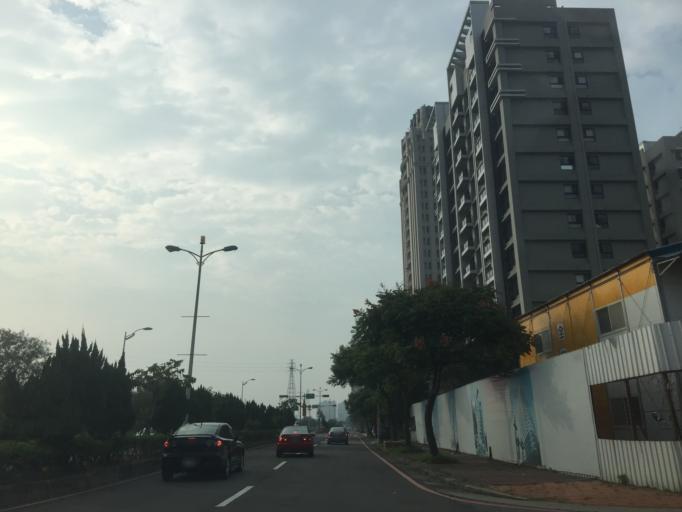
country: TW
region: Taiwan
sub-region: Hsinchu
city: Zhubei
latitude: 24.8173
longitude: 121.0122
